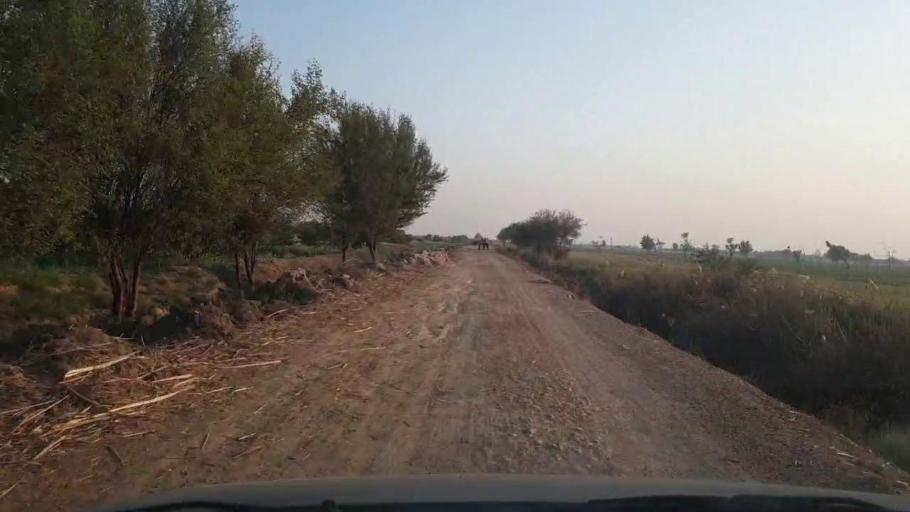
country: PK
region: Sindh
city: Mirwah Gorchani
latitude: 25.3548
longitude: 69.1530
